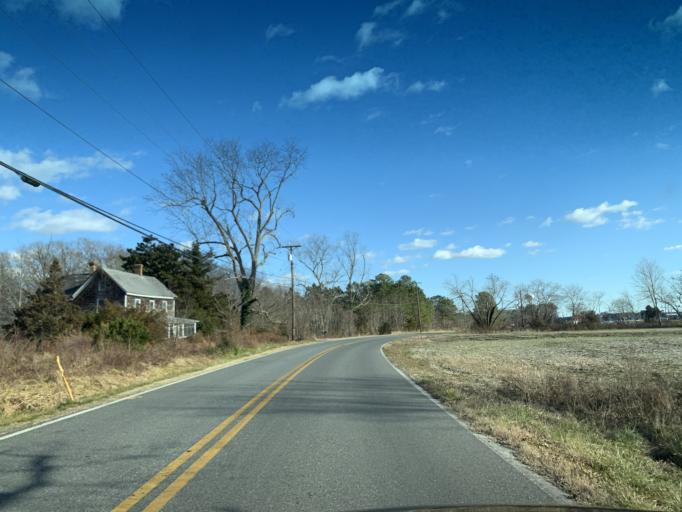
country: US
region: Maryland
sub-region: Worcester County
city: Ocean Pines
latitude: 38.3486
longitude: -75.1707
